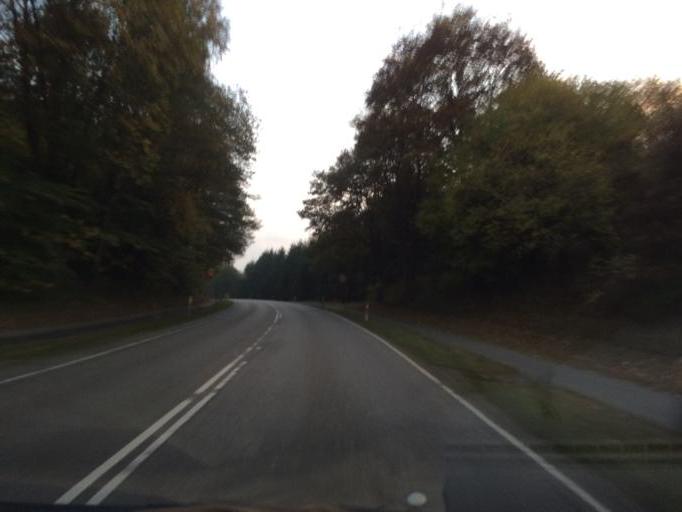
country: DK
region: Central Jutland
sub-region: Silkeborg Kommune
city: Silkeborg
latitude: 56.1571
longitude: 9.4995
